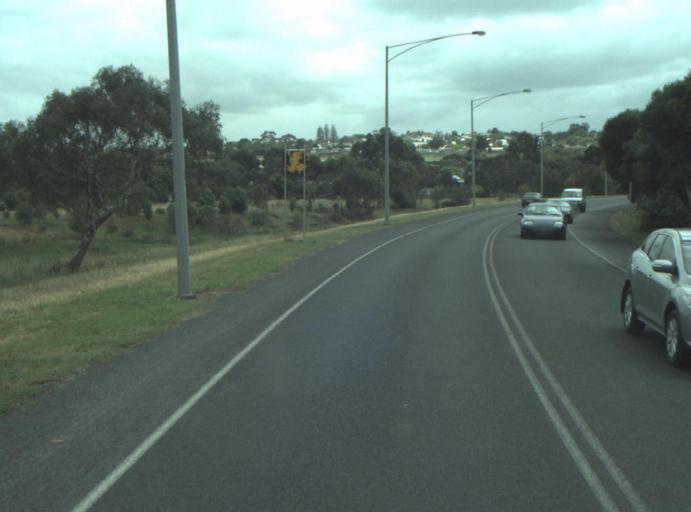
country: AU
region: Victoria
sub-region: Greater Geelong
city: Wandana Heights
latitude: -38.1645
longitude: 144.3293
